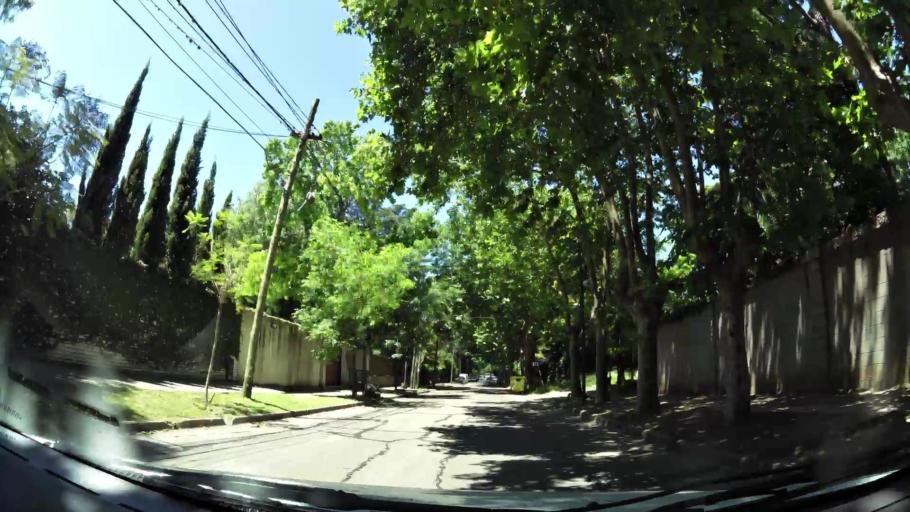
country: AR
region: Buenos Aires
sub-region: Partido de San Isidro
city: San Isidro
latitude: -34.4959
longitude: -58.5617
